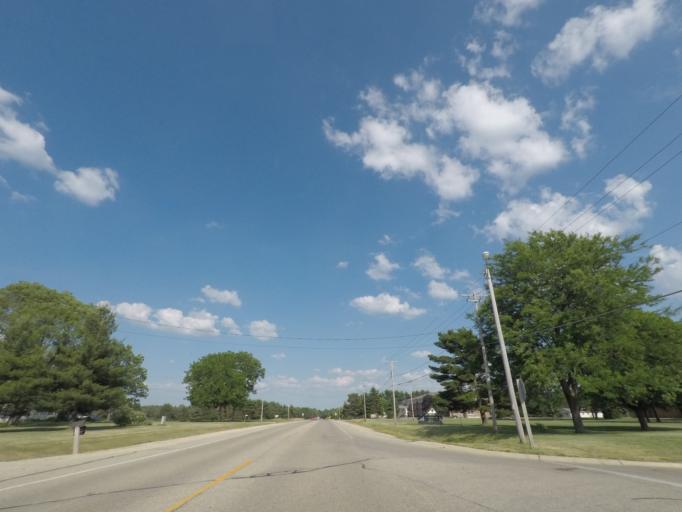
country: US
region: Wisconsin
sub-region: Walworth County
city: East Troy
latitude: 42.7921
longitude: -88.4232
